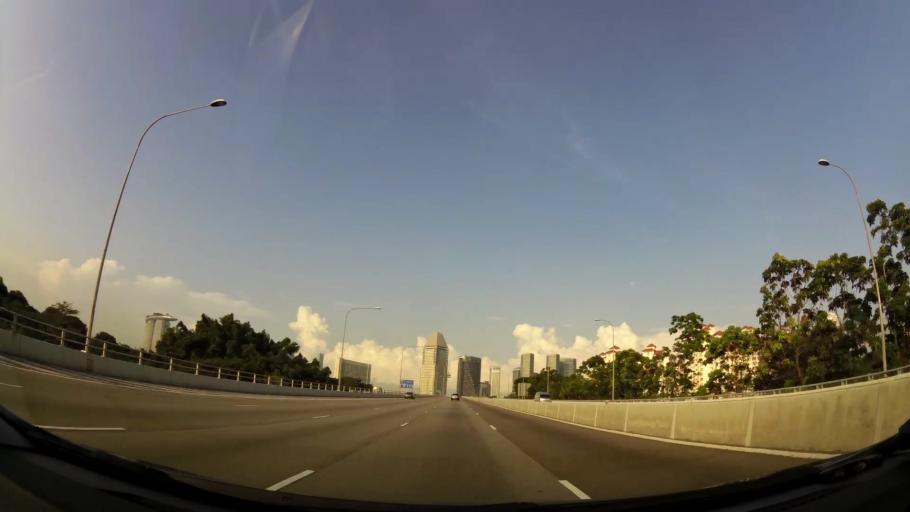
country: SG
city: Singapore
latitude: 1.2950
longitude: 103.8698
